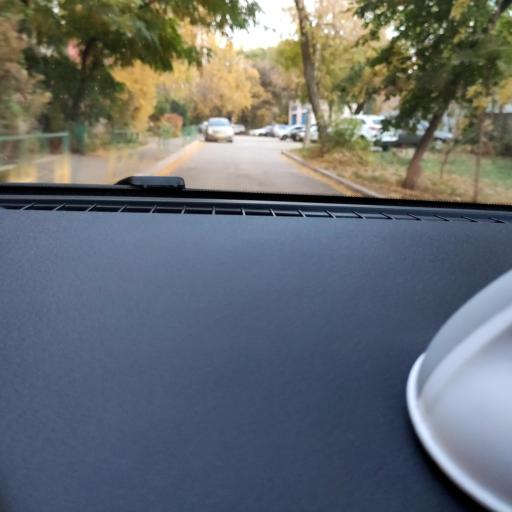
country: RU
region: Samara
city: Samara
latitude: 53.2139
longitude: 50.1341
